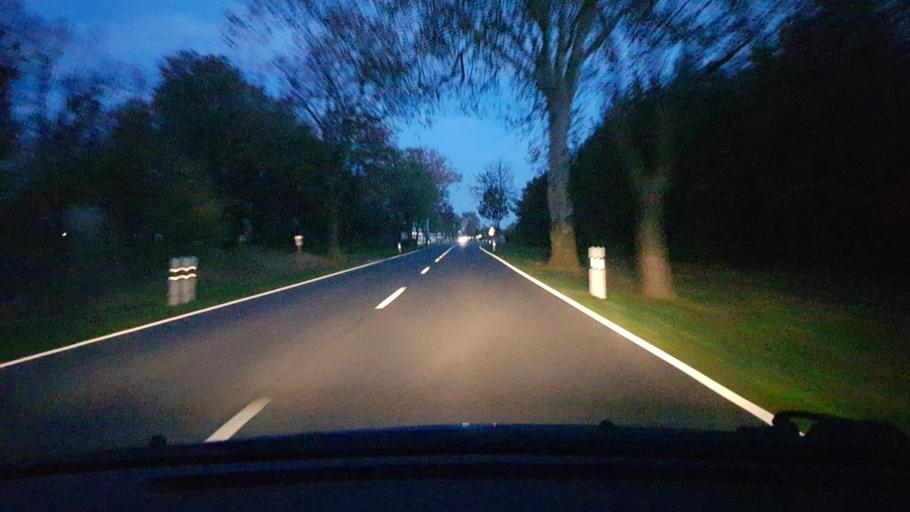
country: DE
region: Saxony-Anhalt
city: Rodleben
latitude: 51.9048
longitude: 12.2076
